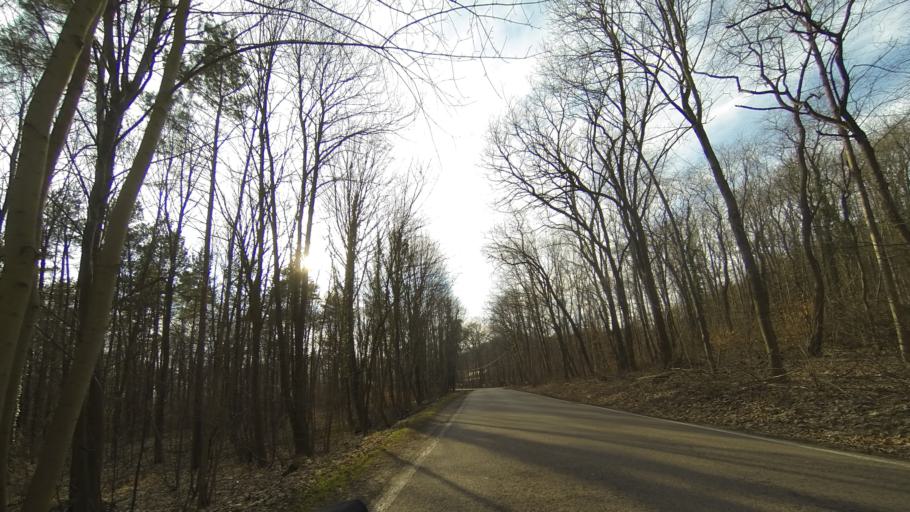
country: DE
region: Saxony
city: Radebeul
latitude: 51.1116
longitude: 13.6956
